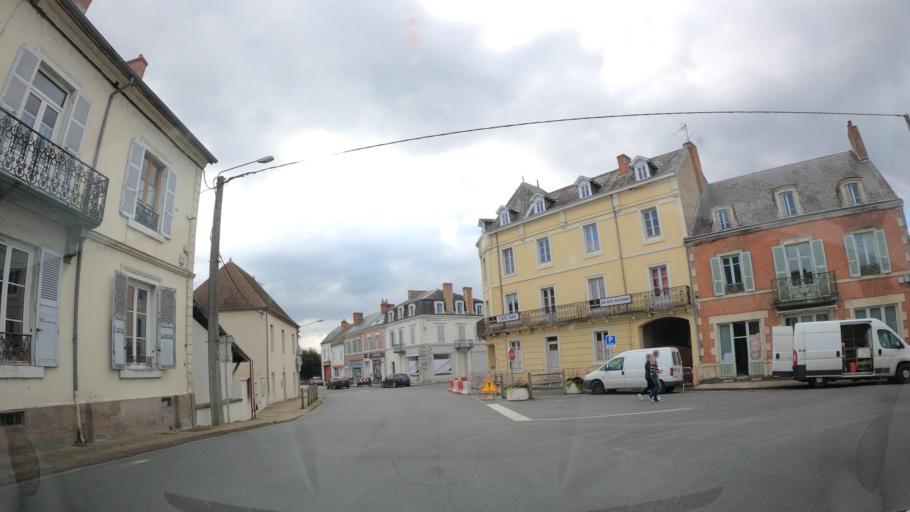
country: FR
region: Auvergne
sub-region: Departement de l'Allier
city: Lapalisse
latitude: 46.3802
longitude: 3.5918
